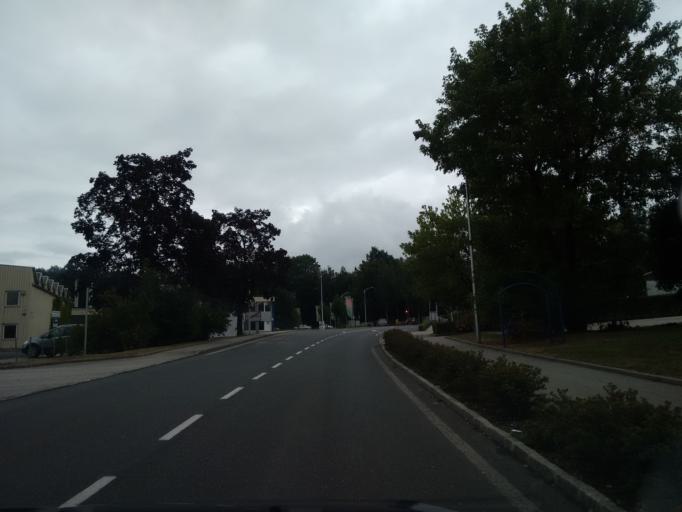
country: AT
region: Upper Austria
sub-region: Politischer Bezirk Grieskirchen
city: Grieskirchen
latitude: 48.2327
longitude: 13.8286
